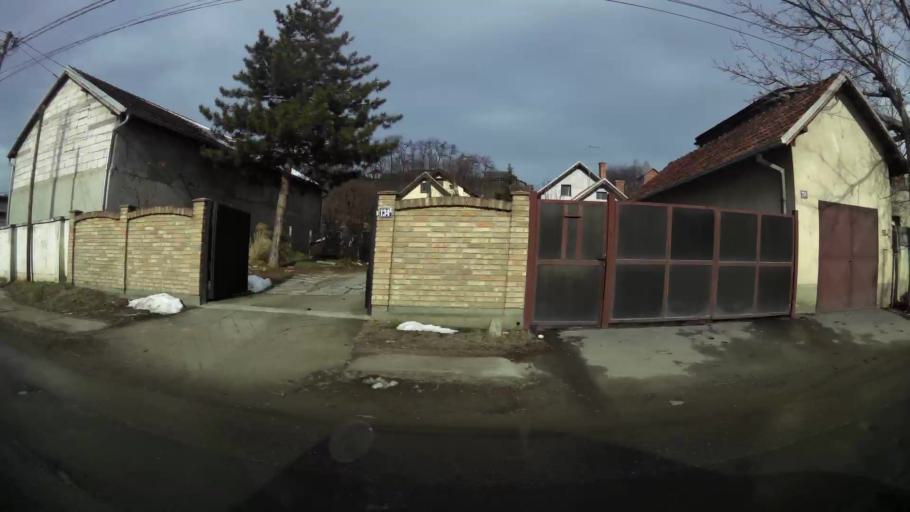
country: RS
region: Central Serbia
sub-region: Belgrade
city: Zemun
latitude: 44.7985
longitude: 20.3521
